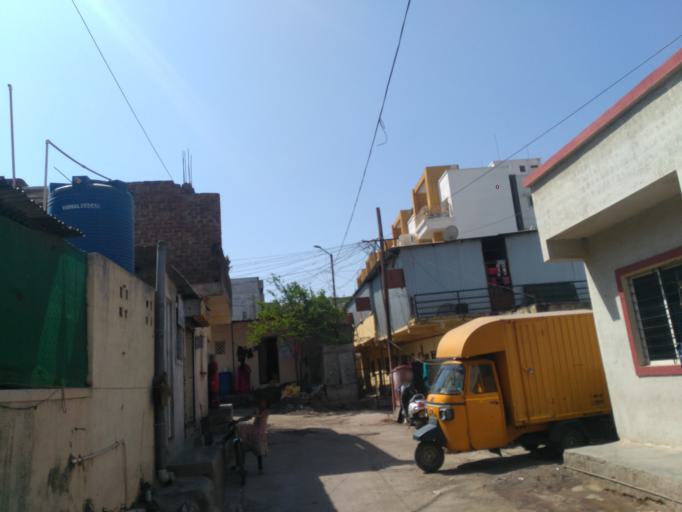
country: IN
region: Maharashtra
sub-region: Pune Division
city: Pune
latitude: 18.4464
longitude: 73.8772
